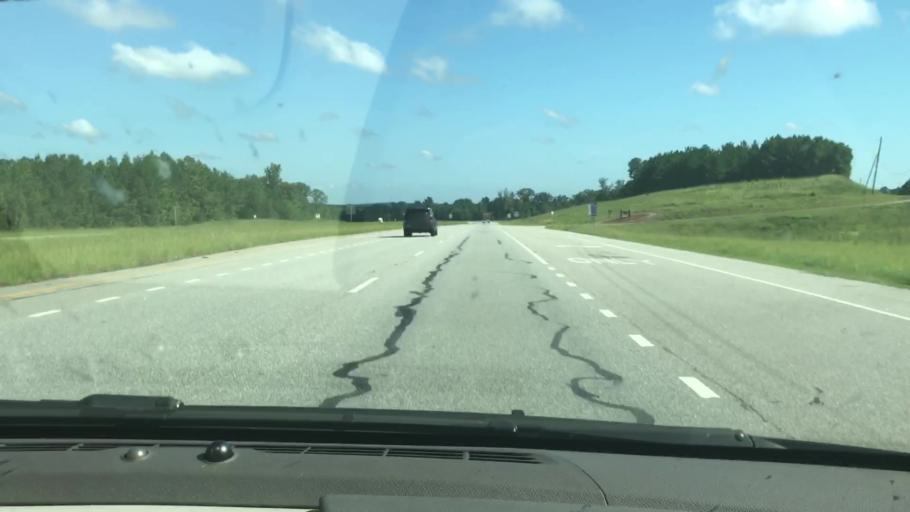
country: US
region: Alabama
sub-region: Barbour County
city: Eufaula
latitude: 32.1648
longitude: -85.1767
